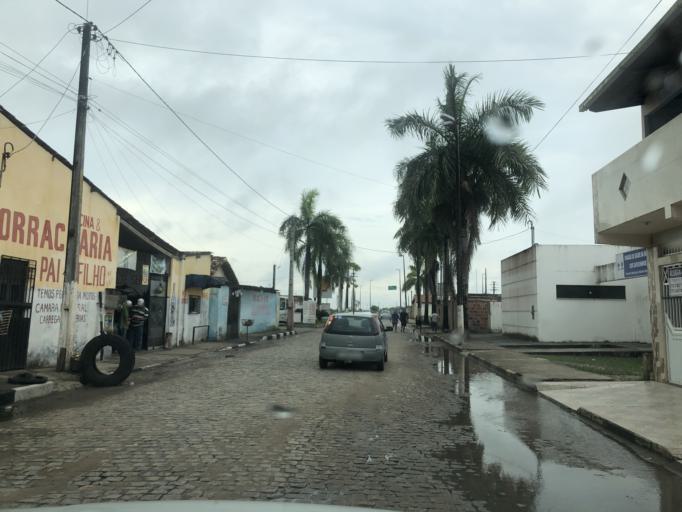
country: BR
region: Bahia
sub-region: Esplanada
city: Esplanada
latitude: -11.7955
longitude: -37.9540
